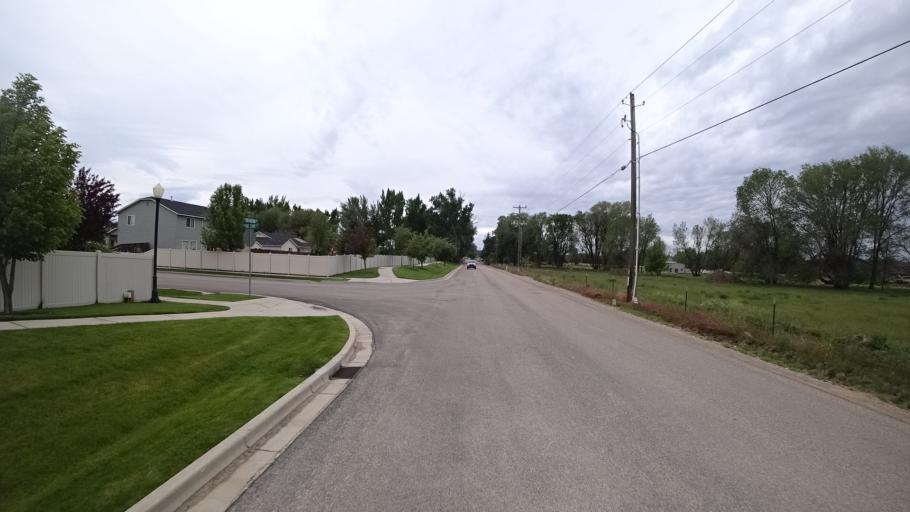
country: US
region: Idaho
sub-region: Ada County
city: Star
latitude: 43.7094
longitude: -116.4883
